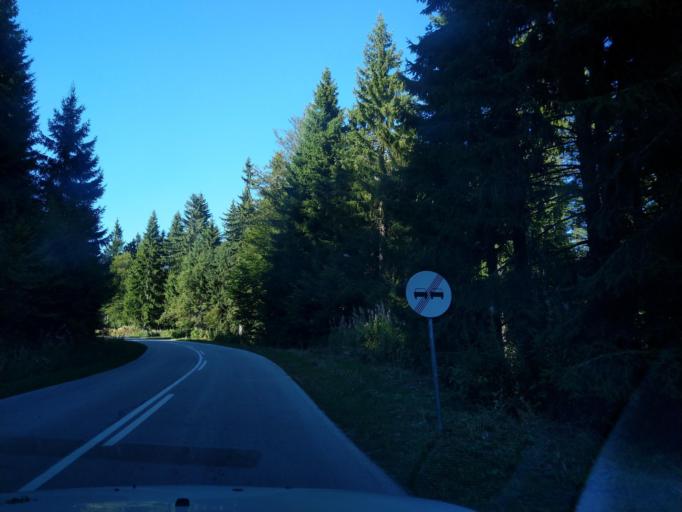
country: RS
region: Central Serbia
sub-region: Moravicki Okrug
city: Ivanjica
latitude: 43.4109
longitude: 20.2662
